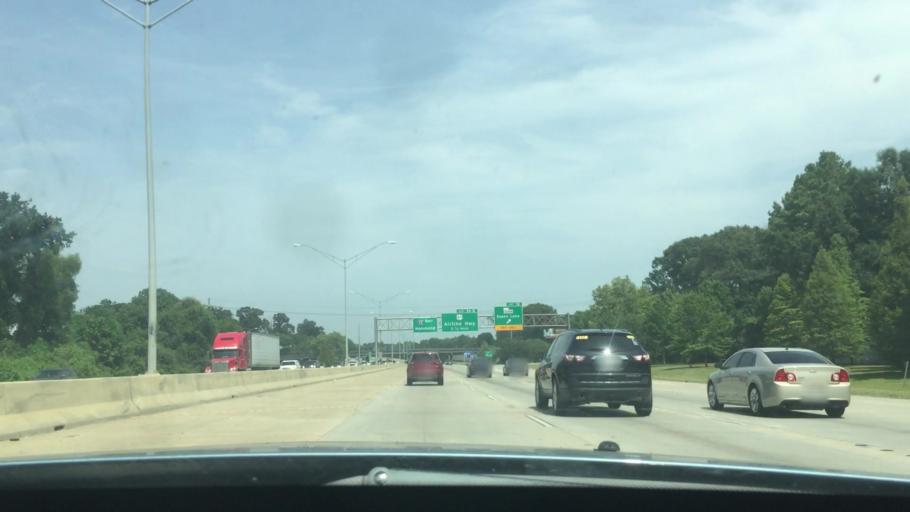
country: US
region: Louisiana
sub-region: East Baton Rouge Parish
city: Westminster
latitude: 30.4176
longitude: -91.1024
